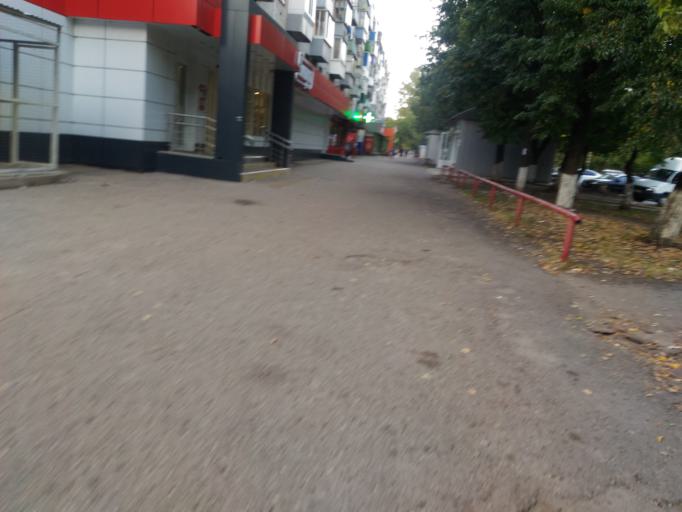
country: RU
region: Ulyanovsk
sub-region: Ulyanovskiy Rayon
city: Ulyanovsk
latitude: 54.3001
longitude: 48.3297
